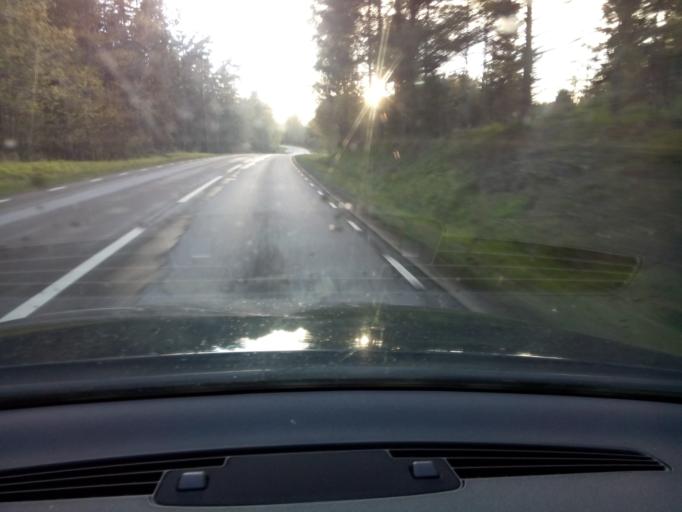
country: SE
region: Soedermanland
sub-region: Oxelosunds Kommun
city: Oxelosund
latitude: 58.7393
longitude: 17.2074
